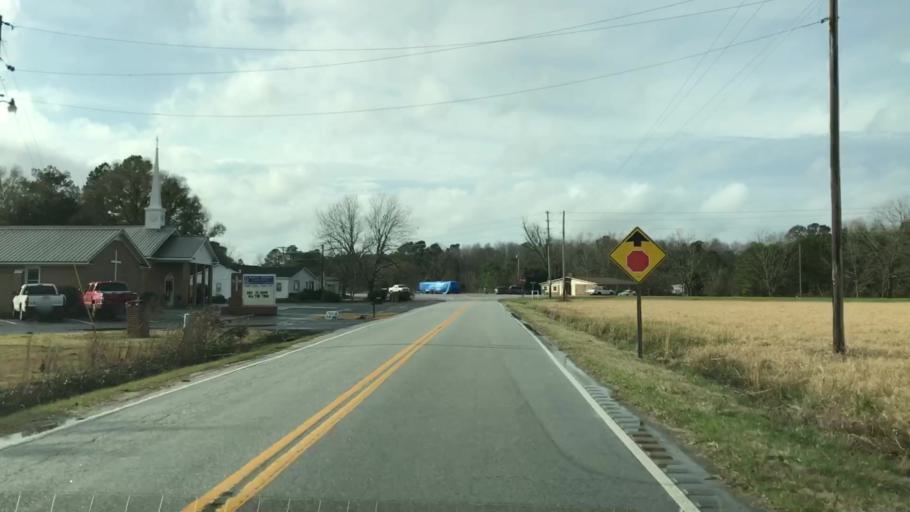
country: US
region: South Carolina
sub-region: Williamsburg County
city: Andrews
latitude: 33.5029
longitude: -79.5234
